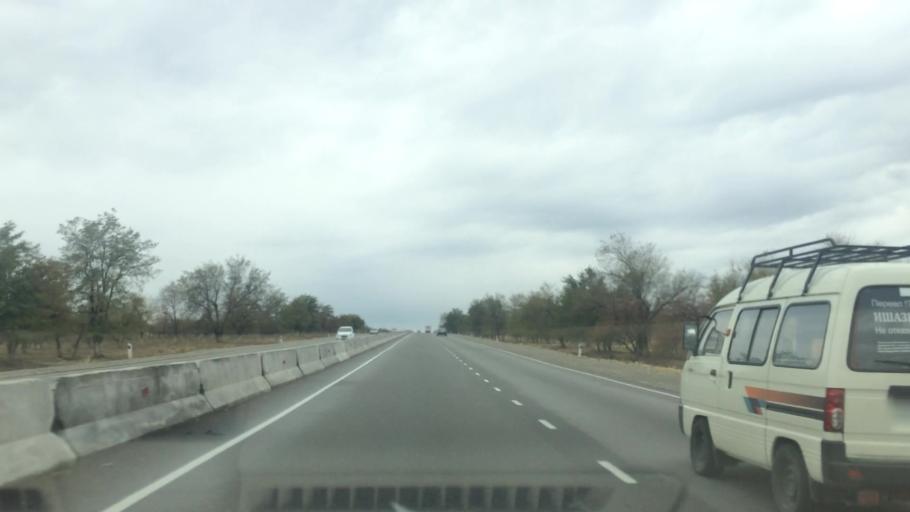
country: UZ
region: Samarqand
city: Bulung'ur
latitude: 39.9337
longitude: 67.5239
